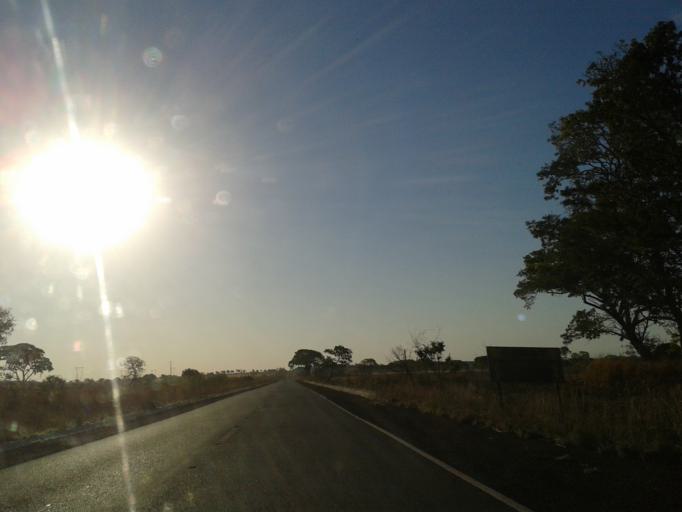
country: BR
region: Minas Gerais
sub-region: Santa Vitoria
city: Santa Vitoria
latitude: -19.1086
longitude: -50.3208
